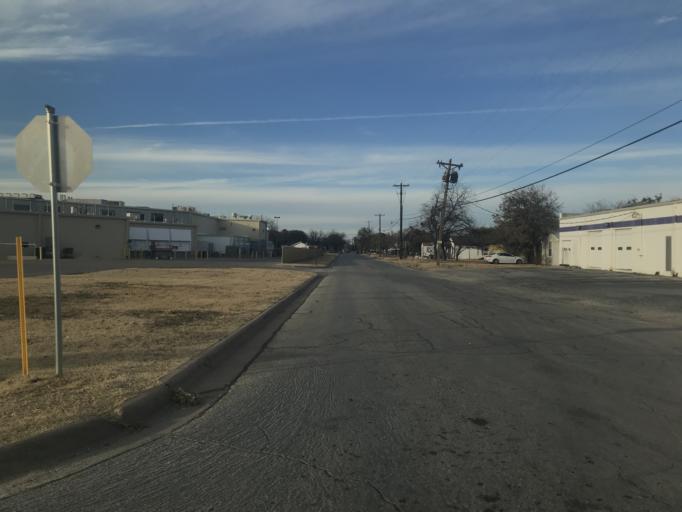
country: US
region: Texas
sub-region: Taylor County
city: Abilene
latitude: 32.4323
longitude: -99.7572
